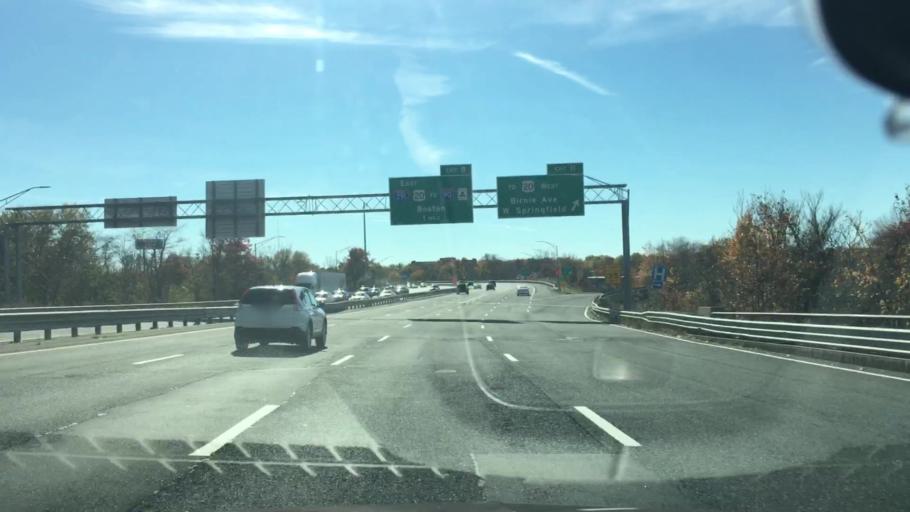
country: US
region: Massachusetts
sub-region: Hampden County
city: West Springfield
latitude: 42.1226
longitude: -72.6085
